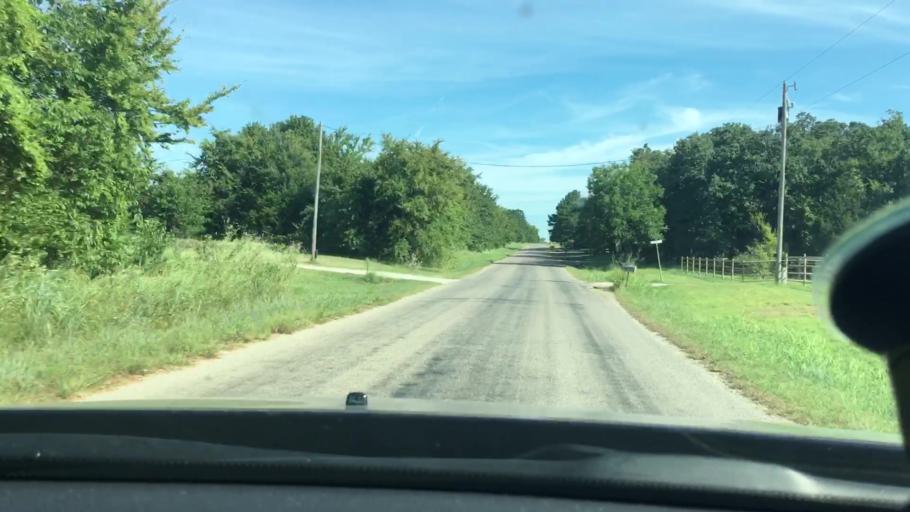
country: US
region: Oklahoma
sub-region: Carter County
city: Lone Grove
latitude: 34.2468
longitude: -97.2475
